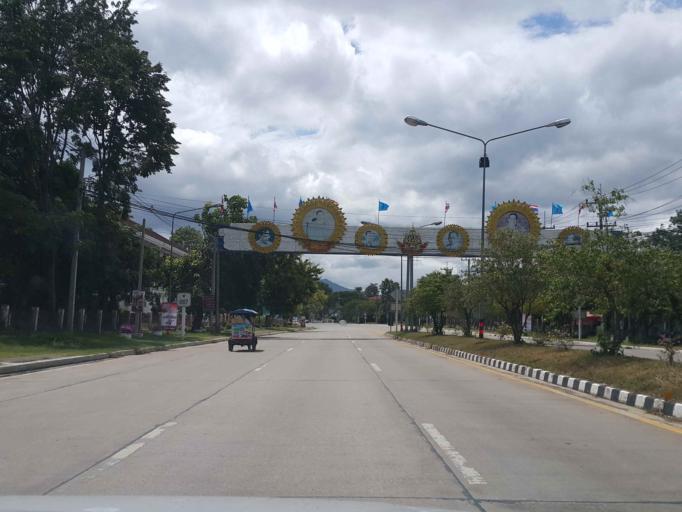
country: TH
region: Tak
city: Tak
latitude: 16.8854
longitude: 99.1261
